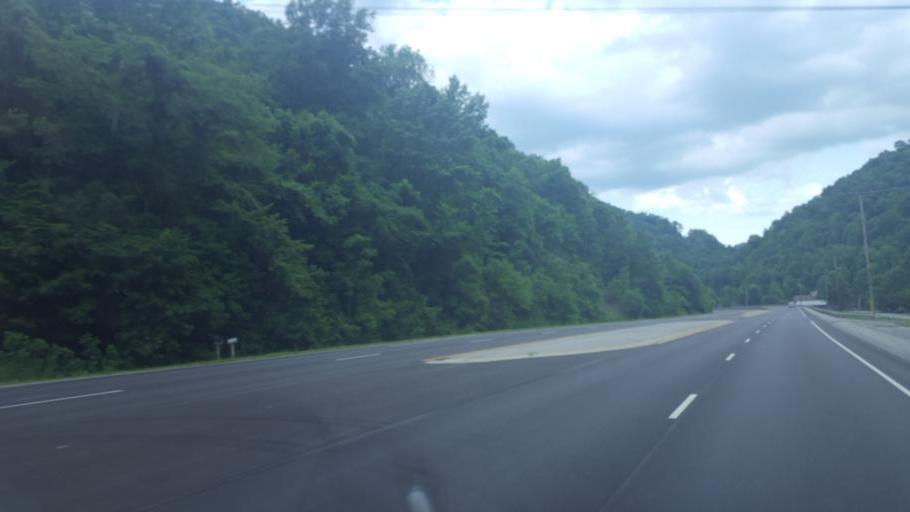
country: US
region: Kentucky
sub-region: Pike County
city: Pikeville
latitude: 37.3293
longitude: -82.5589
